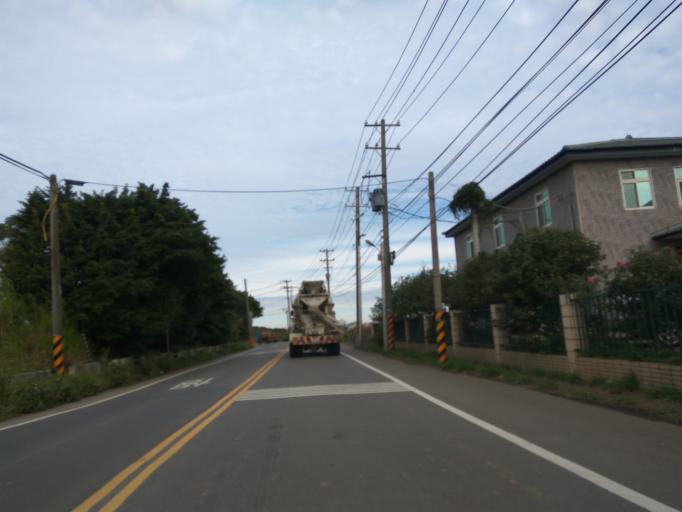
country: TW
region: Taiwan
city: Daxi
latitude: 24.9420
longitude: 121.1550
